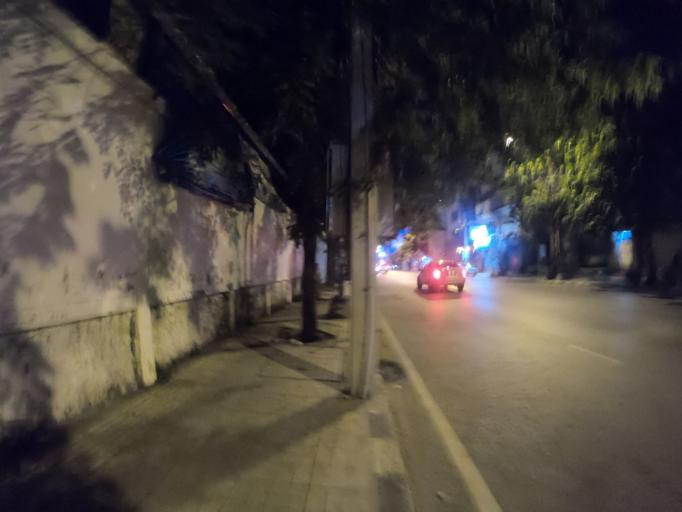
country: TH
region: Khon Kaen
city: Khon Kaen
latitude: 16.4319
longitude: 102.8341
